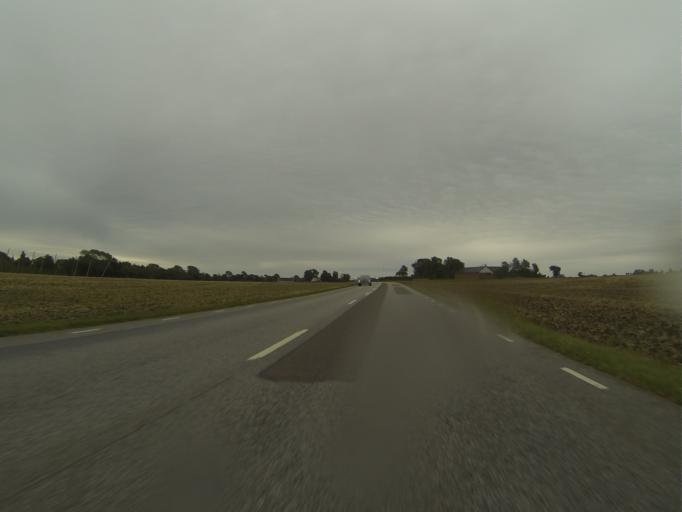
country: SE
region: Skane
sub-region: Svedala Kommun
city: Klagerup
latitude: 55.6349
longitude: 13.2841
